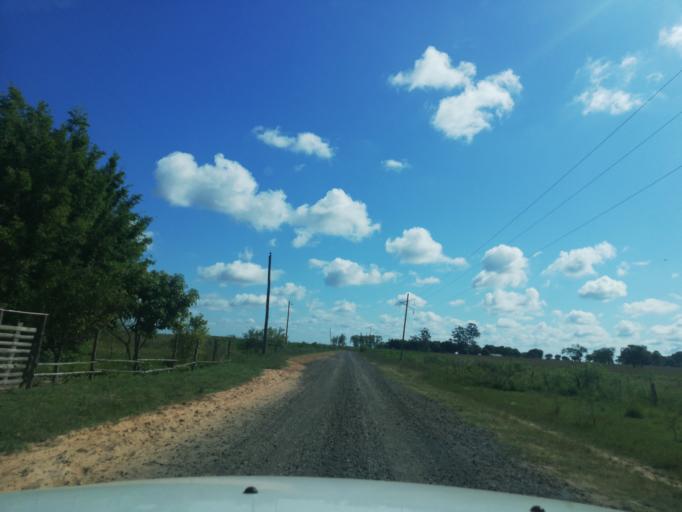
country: AR
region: Corrientes
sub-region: Departamento de San Miguel
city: San Miguel
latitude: -27.9844
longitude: -57.5829
